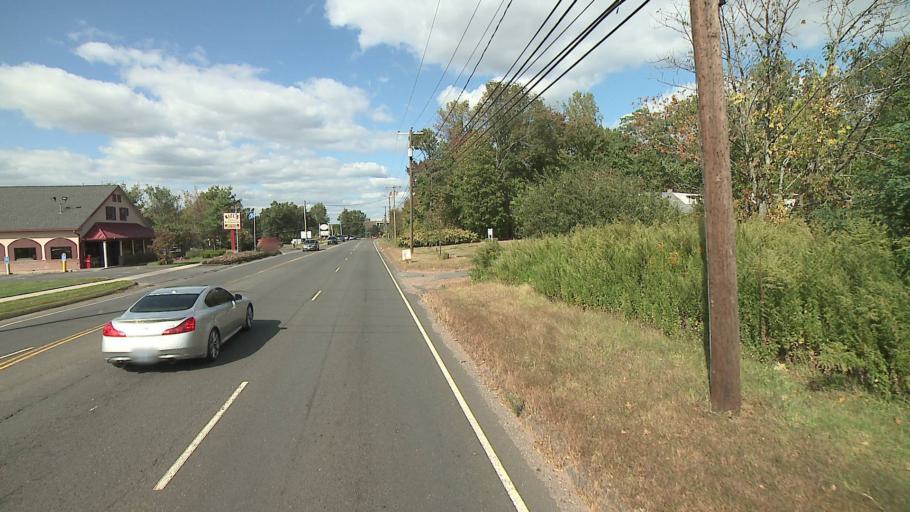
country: US
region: Connecticut
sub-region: Hartford County
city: Plainville
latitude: 41.6429
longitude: -72.9013
